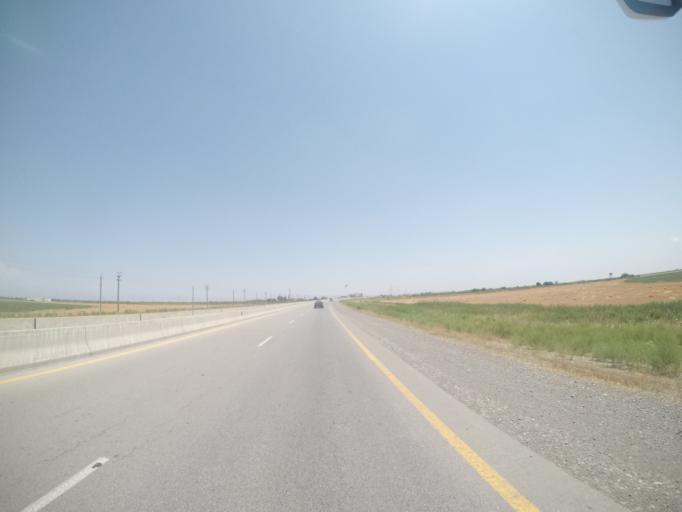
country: AZ
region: Kurdamir Rayon
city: Kyurdarmir
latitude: 40.3191
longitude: 48.1804
